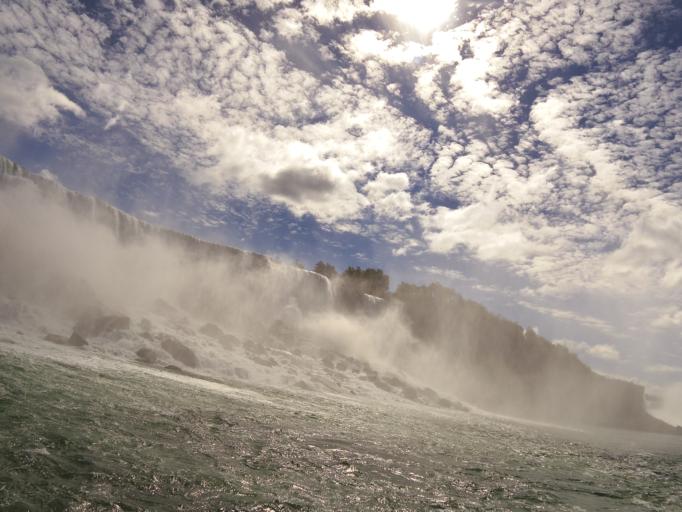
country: CA
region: Ontario
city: Niagara Falls
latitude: 43.0862
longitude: -79.0713
